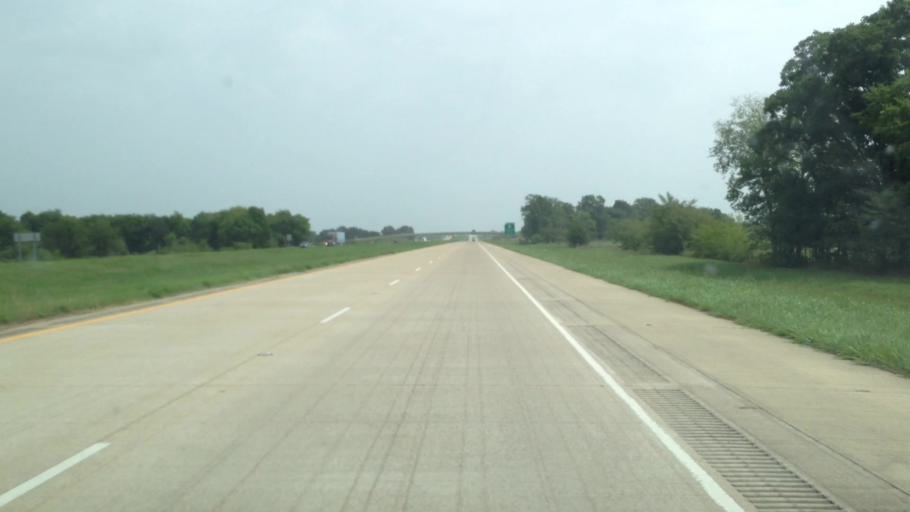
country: US
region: Louisiana
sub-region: Caddo Parish
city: Vivian
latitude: 32.8373
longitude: -93.8715
